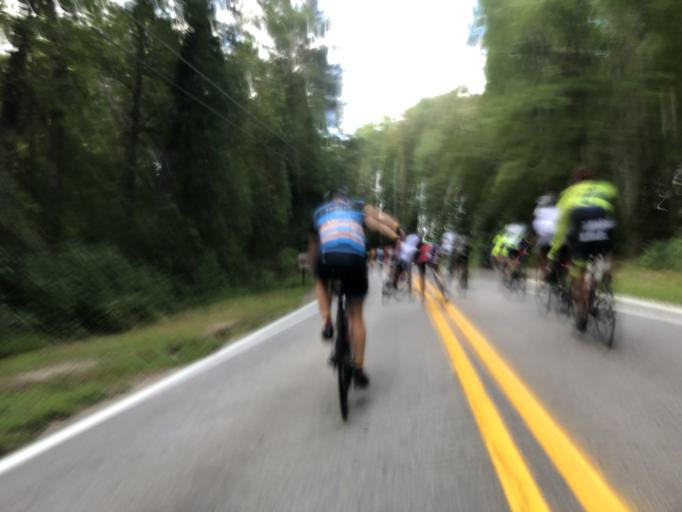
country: US
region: Georgia
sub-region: Fulton County
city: Palmetto
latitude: 33.5925
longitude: -84.6537
